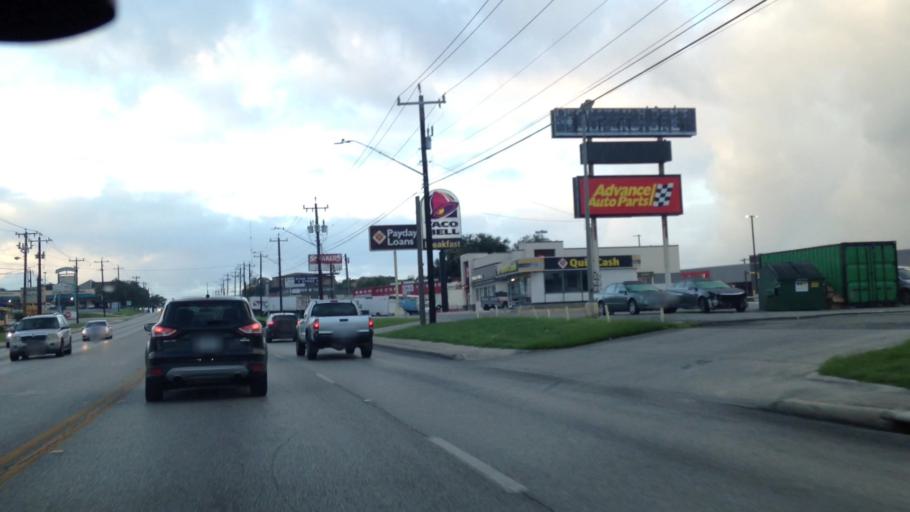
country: US
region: Texas
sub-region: Bexar County
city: Windcrest
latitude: 29.5443
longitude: -98.4111
